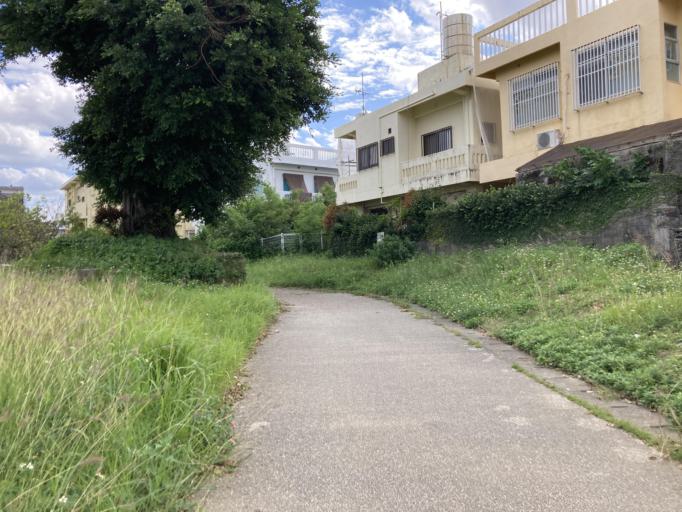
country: JP
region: Okinawa
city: Naha-shi
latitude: 26.2089
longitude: 127.6846
